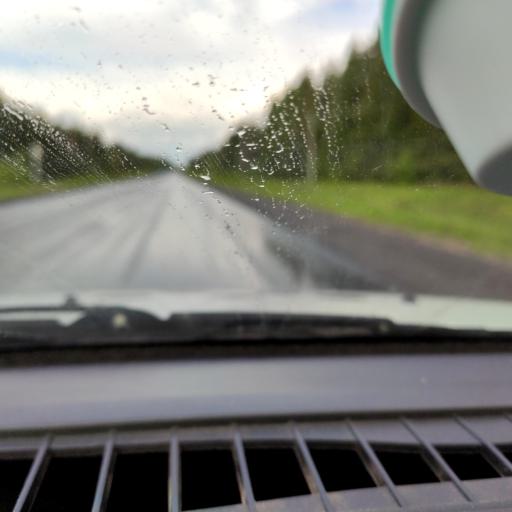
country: RU
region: Perm
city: Orda
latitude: 57.2167
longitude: 56.9442
